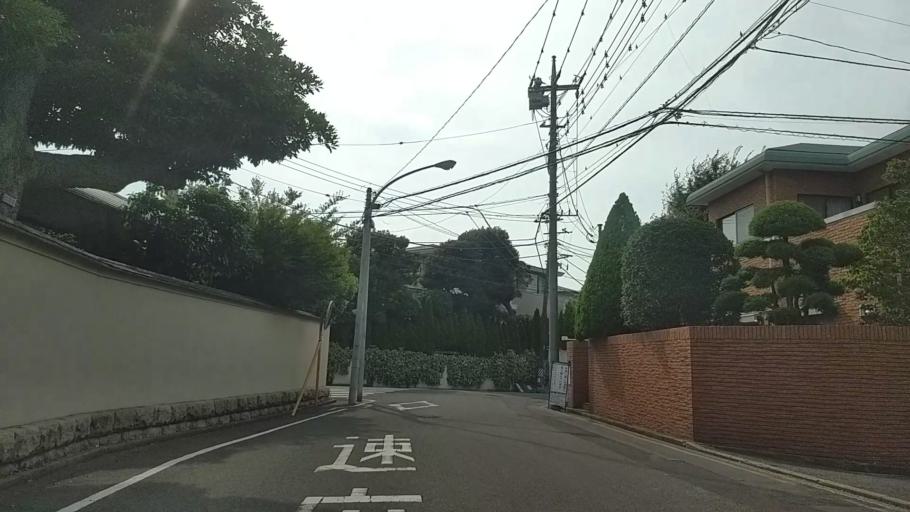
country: JP
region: Kanagawa
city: Yokohama
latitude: 35.4375
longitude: 139.6570
